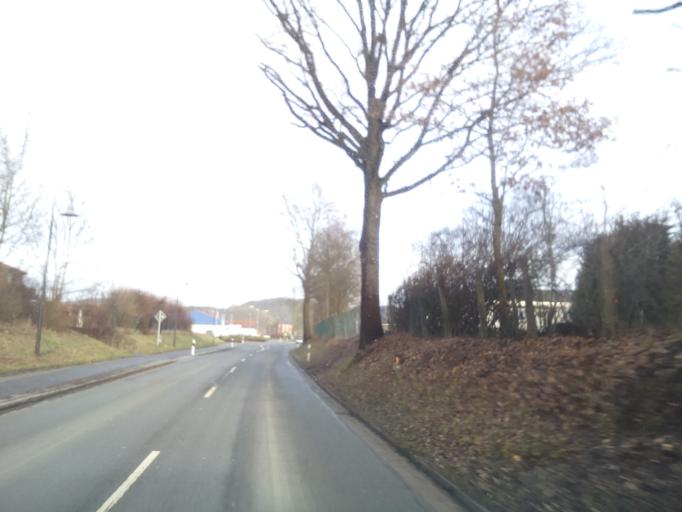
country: DE
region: Bavaria
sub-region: Upper Franconia
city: Neuenmarkt
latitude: 50.0961
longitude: 11.5873
